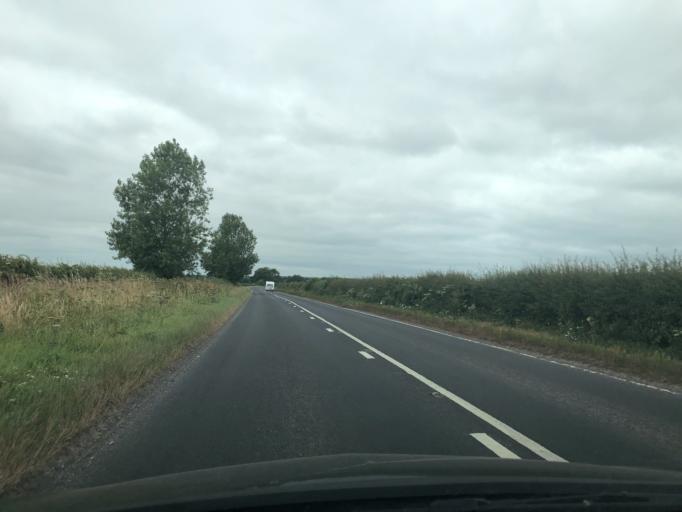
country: GB
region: England
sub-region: North Yorkshire
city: East Ayton
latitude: 54.2491
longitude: -0.4617
